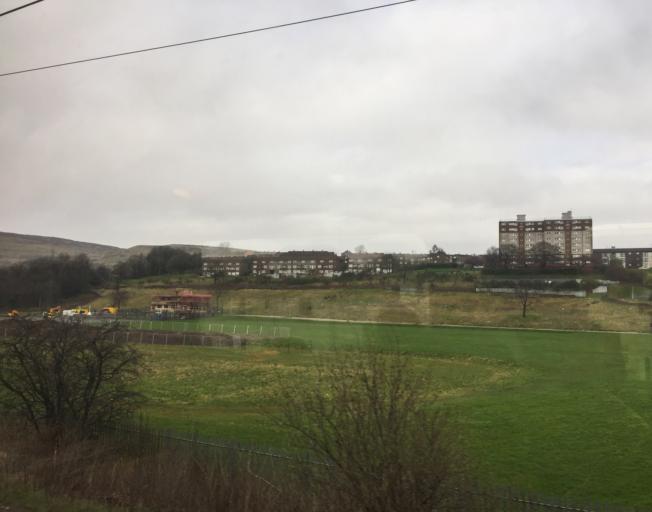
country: GB
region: Scotland
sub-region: West Dunbartonshire
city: Old Kilpatrick
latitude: 55.9162
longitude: -4.4371
